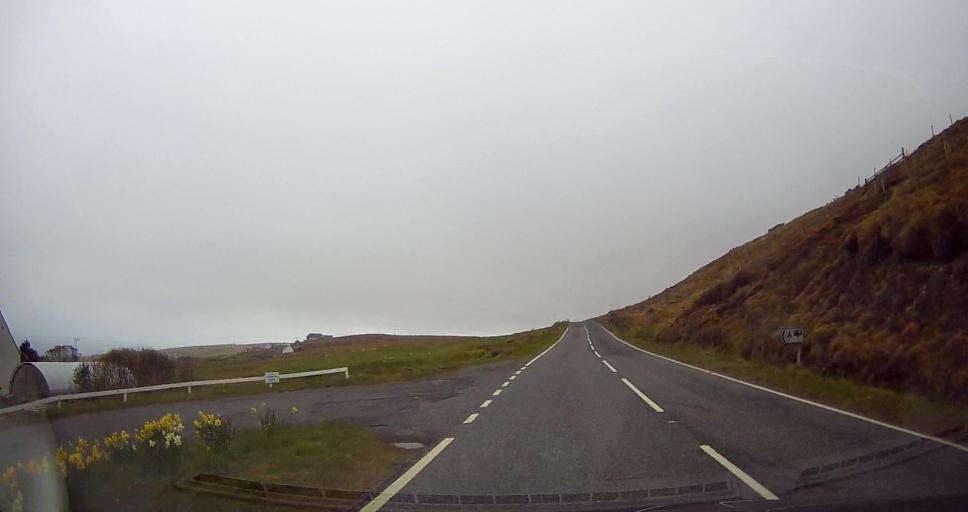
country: GB
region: Scotland
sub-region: Shetland Islands
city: Sandwick
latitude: 59.9720
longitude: -1.2780
